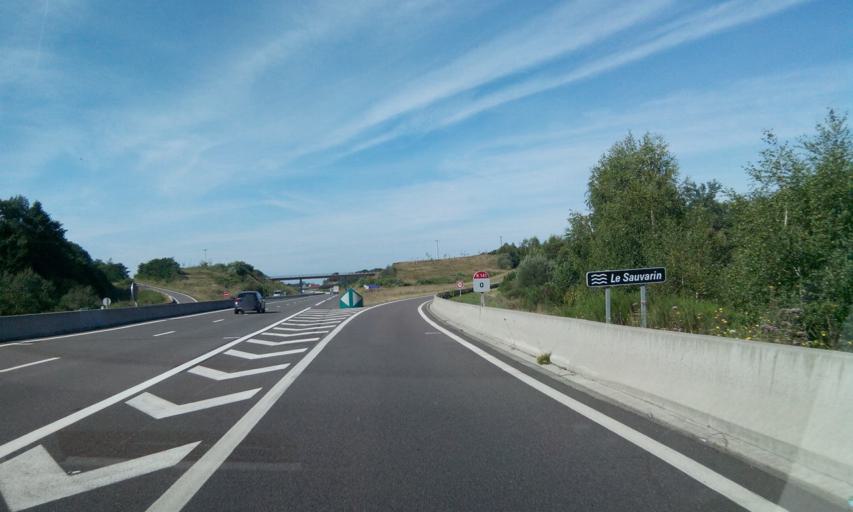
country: FR
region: Poitou-Charentes
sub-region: Departement de la Charente
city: Etagnac
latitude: 45.8919
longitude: 0.8195
